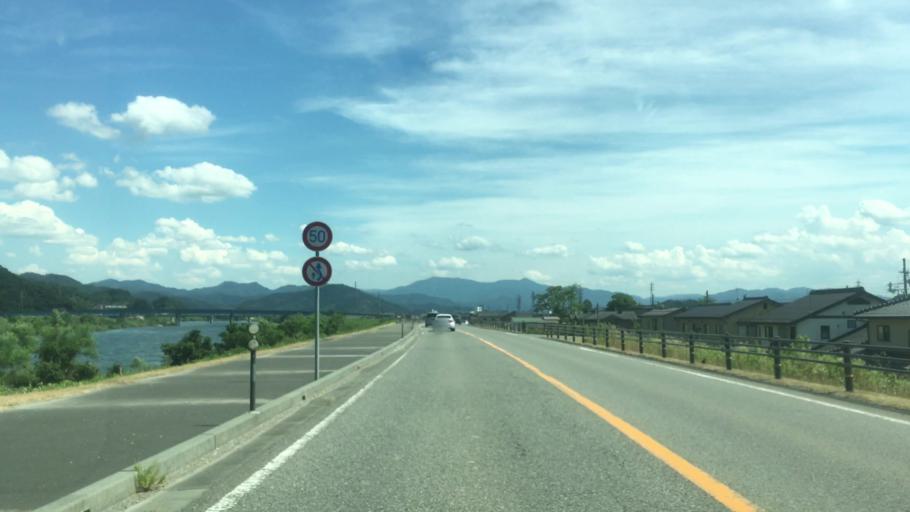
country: JP
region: Hyogo
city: Toyooka
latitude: 35.5623
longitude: 134.8133
